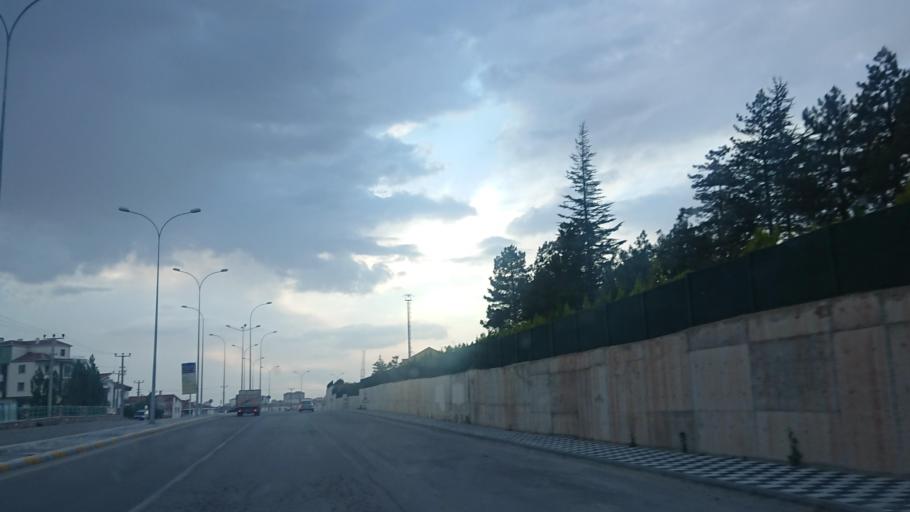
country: TR
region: Aksaray
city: Aksaray
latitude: 38.4024
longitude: 34.0161
